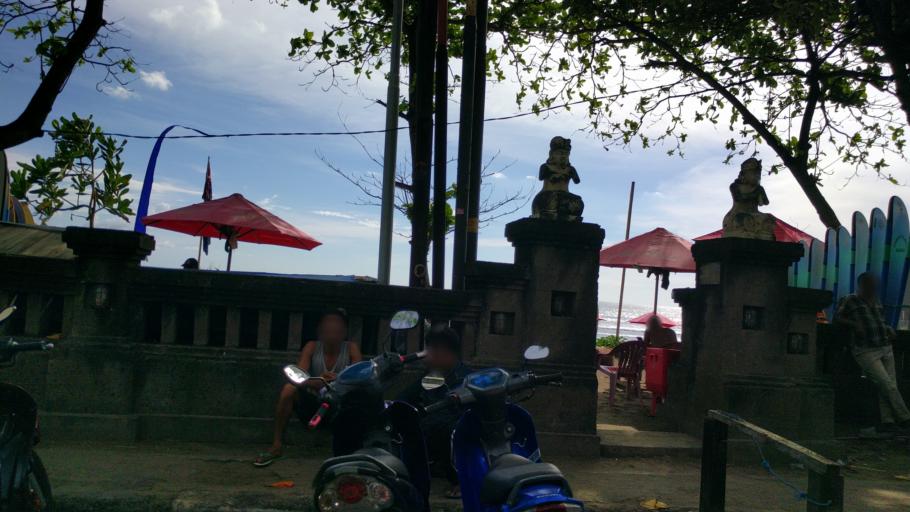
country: ID
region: Bali
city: Kuta
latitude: -8.6964
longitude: 115.1609
